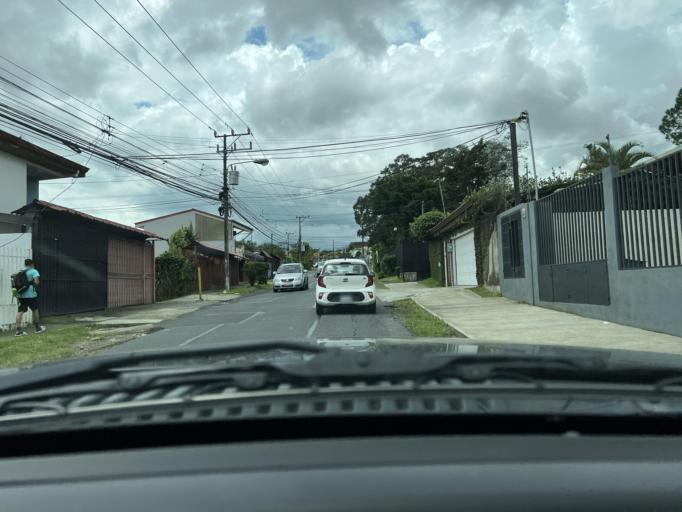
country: CR
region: San Jose
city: Sabanilla
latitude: 9.9325
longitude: -84.0319
